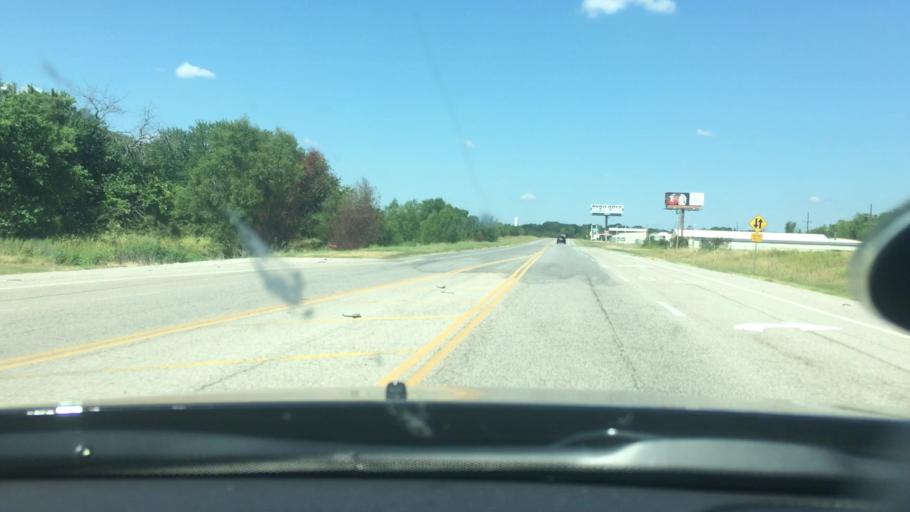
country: US
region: Oklahoma
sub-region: Marshall County
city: Kingston
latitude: 33.9975
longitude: -96.6551
